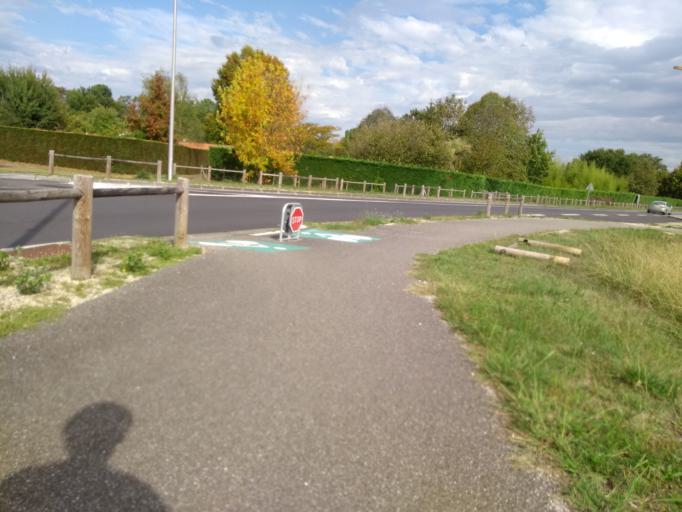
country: FR
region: Aquitaine
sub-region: Departement de la Gironde
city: Cestas
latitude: 44.7407
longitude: -0.6526
